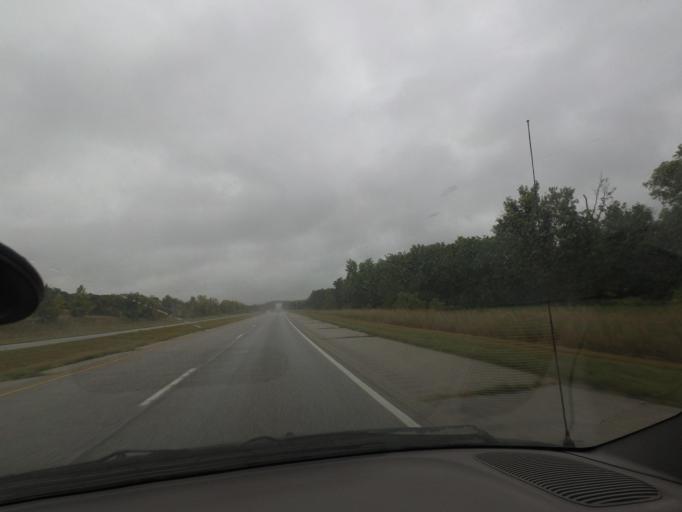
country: US
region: Illinois
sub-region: Pike County
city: Barry
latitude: 39.7216
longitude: -91.1119
